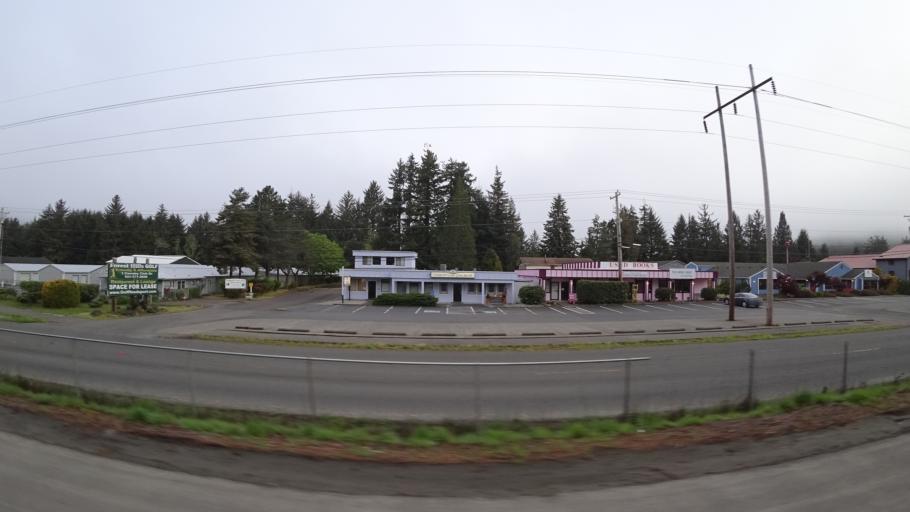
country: US
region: Oregon
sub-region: Douglas County
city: Reedsport
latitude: 43.6939
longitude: -124.1272
